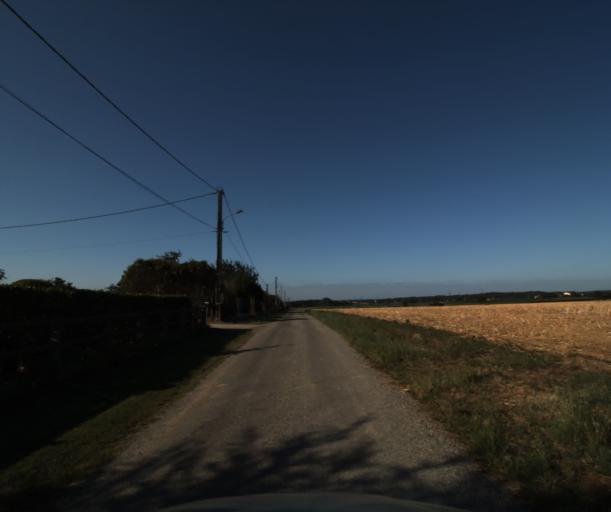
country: FR
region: Midi-Pyrenees
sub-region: Departement de la Haute-Garonne
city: Labarthe-sur-Leze
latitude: 43.4495
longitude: 1.3828
